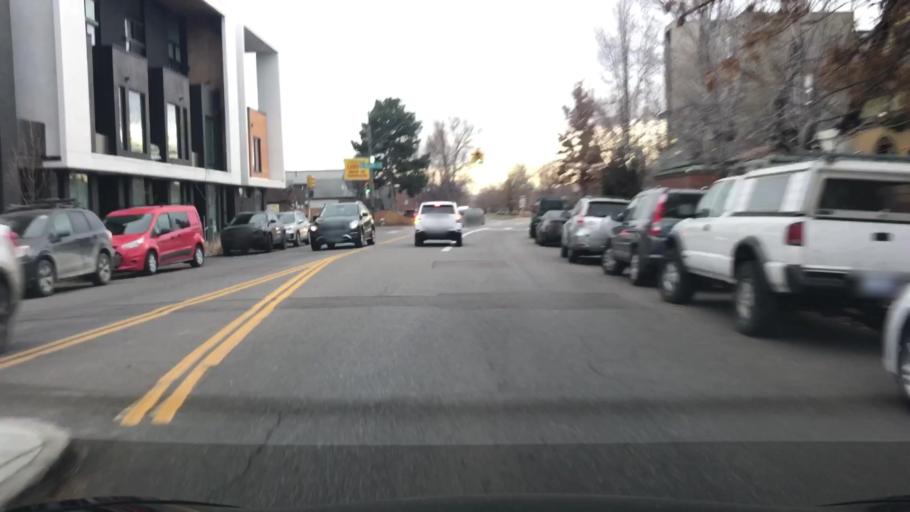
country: US
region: Colorado
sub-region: Denver County
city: Denver
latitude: 39.7153
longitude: -104.9827
